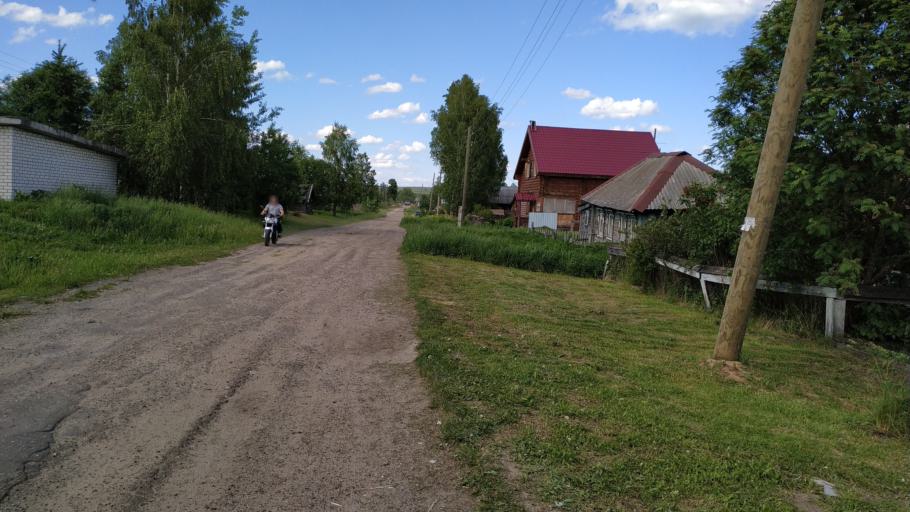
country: RU
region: Nizjnij Novgorod
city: Bogorodsk
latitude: 55.8833
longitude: 43.5562
